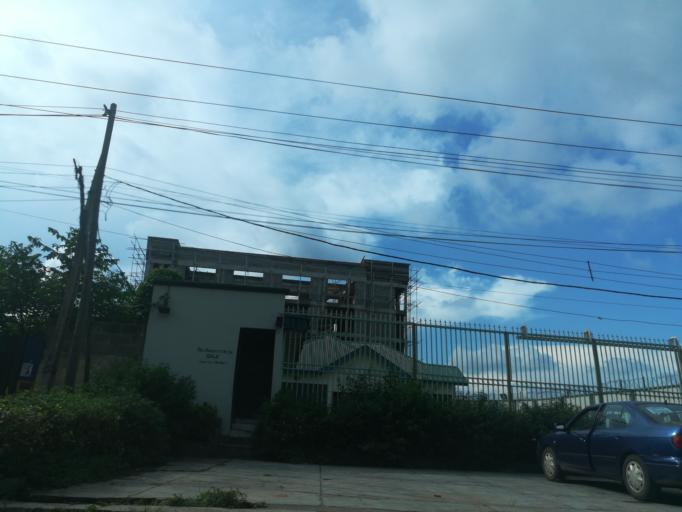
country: NG
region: Lagos
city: Ikeja
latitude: 6.6181
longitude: 3.3609
